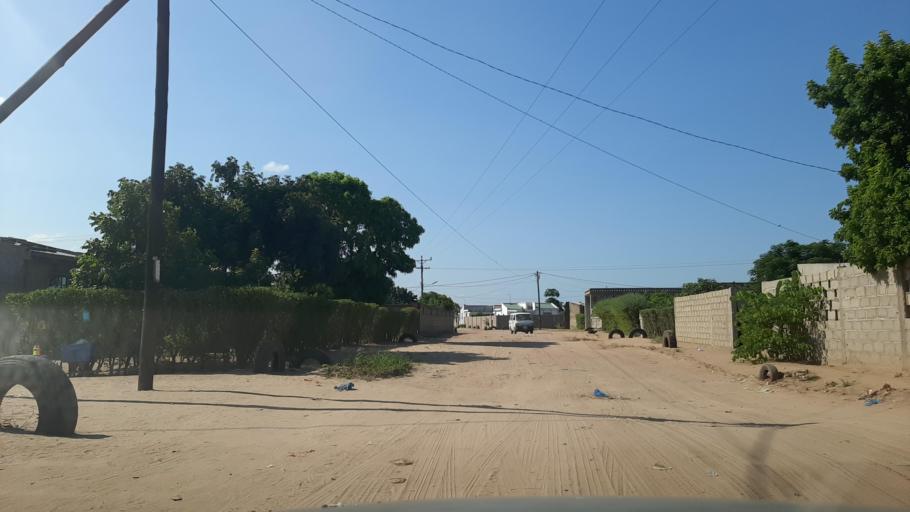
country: MZ
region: Maputo
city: Matola
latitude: -25.8094
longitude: 32.4919
